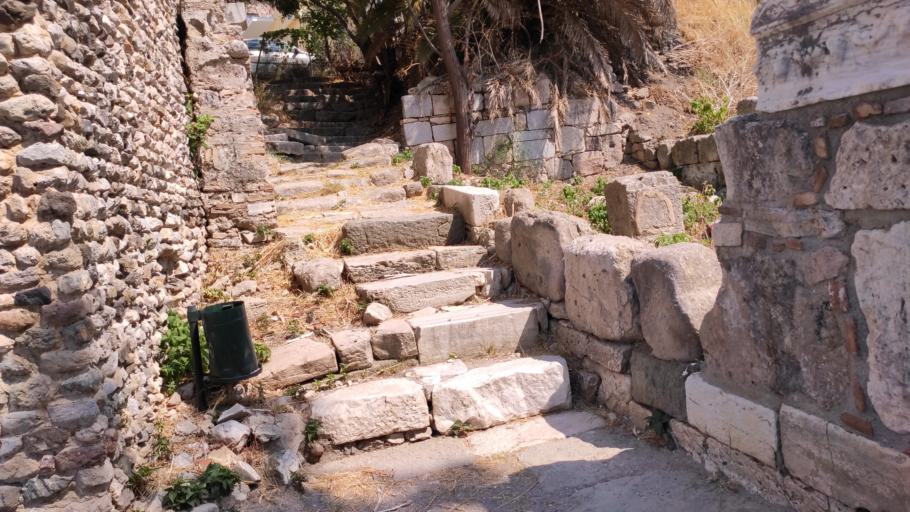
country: GR
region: South Aegean
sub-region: Nomos Dodekanisou
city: Kos
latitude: 36.8913
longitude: 27.2849
